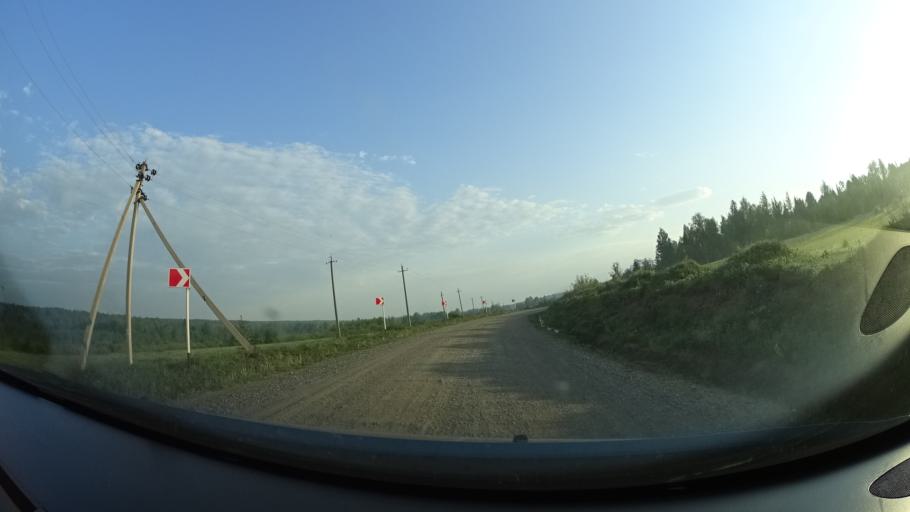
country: RU
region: Perm
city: Barda
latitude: 56.6964
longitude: 55.6812
